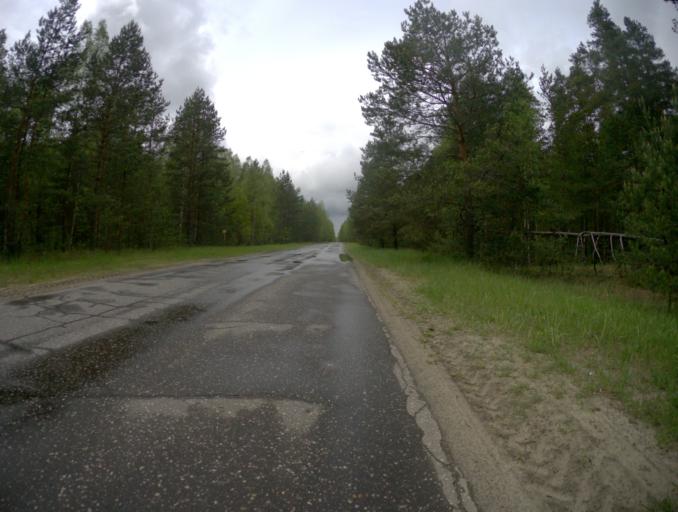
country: RU
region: Vladimir
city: Zolotkovo
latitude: 55.3490
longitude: 40.9382
